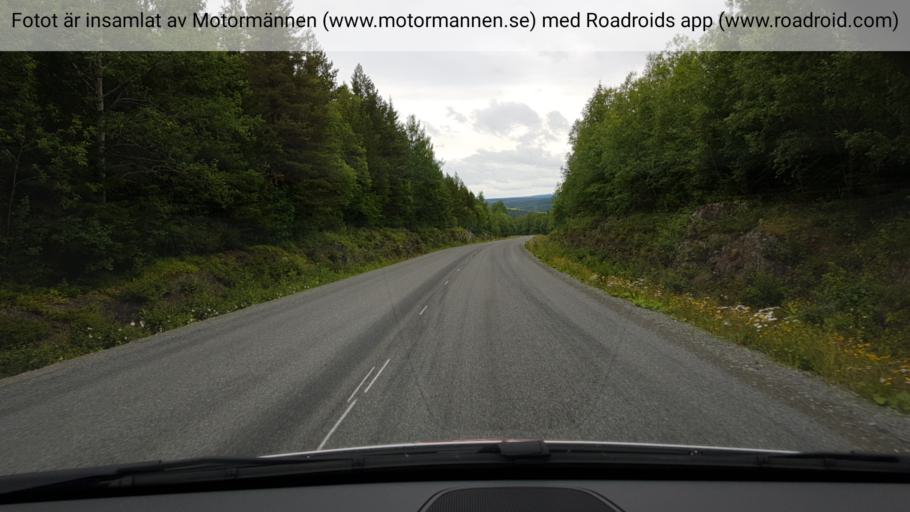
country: SE
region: Jaemtland
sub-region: Krokoms Kommun
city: Krokom
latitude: 63.6686
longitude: 14.5396
